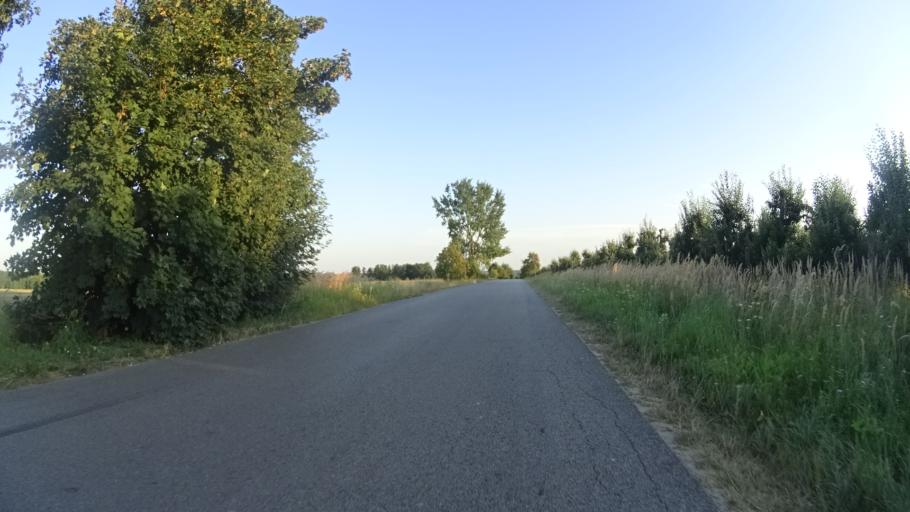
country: PL
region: Masovian Voivodeship
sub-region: Powiat bialobrzeski
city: Wysmierzyce
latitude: 51.6648
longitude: 20.8312
